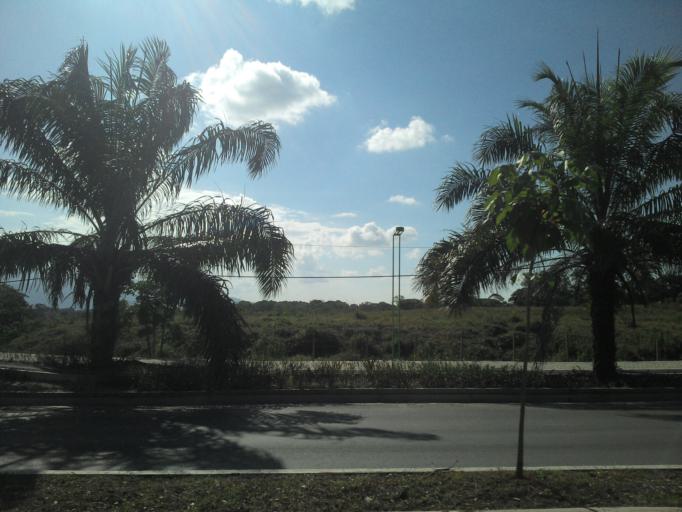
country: MX
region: Chiapas
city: Palenque
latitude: 17.5254
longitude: -91.9923
